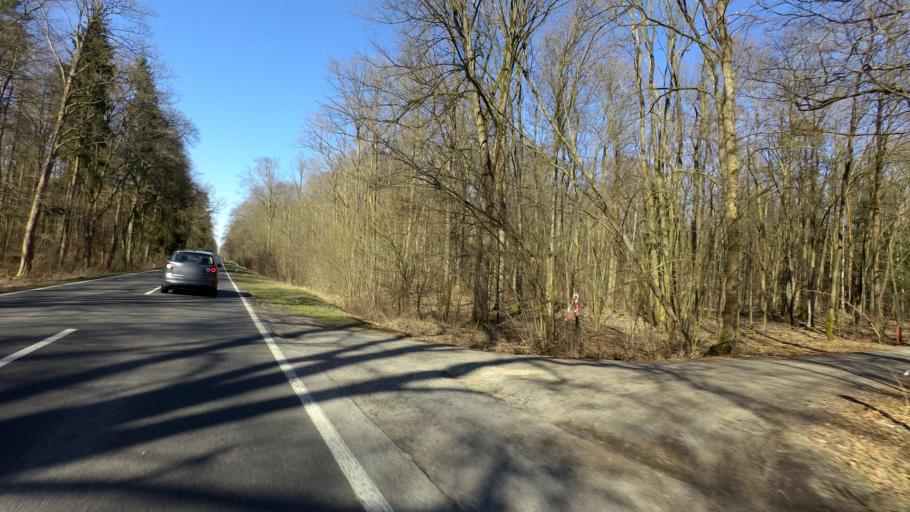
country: DE
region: Brandenburg
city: Eberswalde
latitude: 52.7925
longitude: 13.8378
